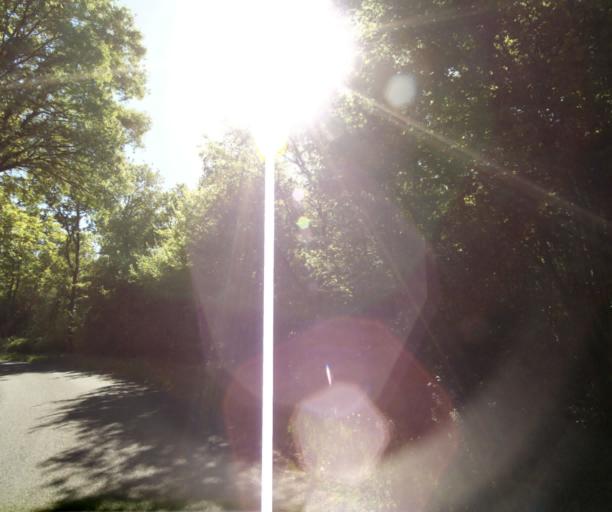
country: FR
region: Poitou-Charentes
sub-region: Departement de la Charente-Maritime
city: Bussac-sur-Charente
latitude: 45.8046
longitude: -0.6660
